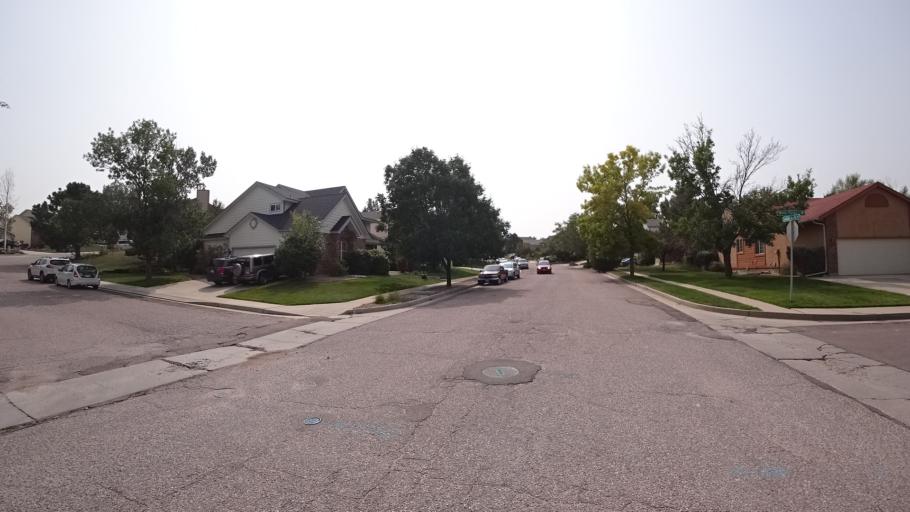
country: US
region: Colorado
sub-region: El Paso County
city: Cimarron Hills
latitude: 38.9198
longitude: -104.7428
